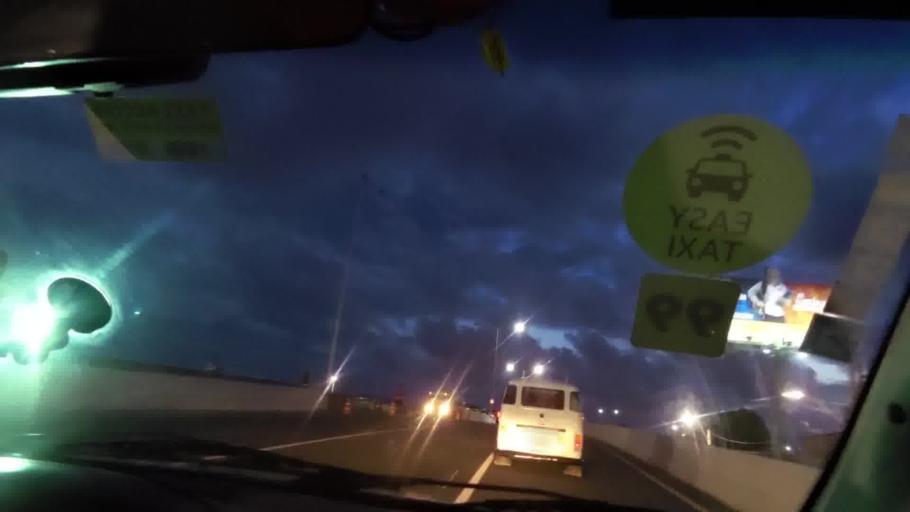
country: BR
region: Pernambuco
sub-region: Recife
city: Recife
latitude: -8.0888
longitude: -34.8917
